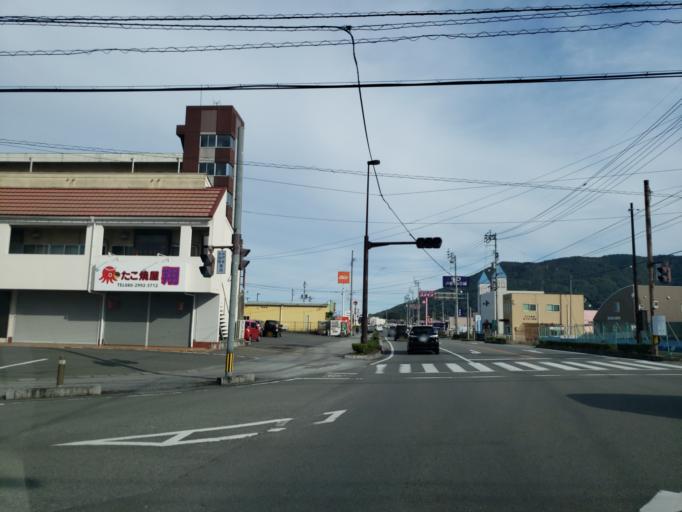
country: JP
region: Tokushima
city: Wakimachi
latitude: 34.0636
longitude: 134.1634
